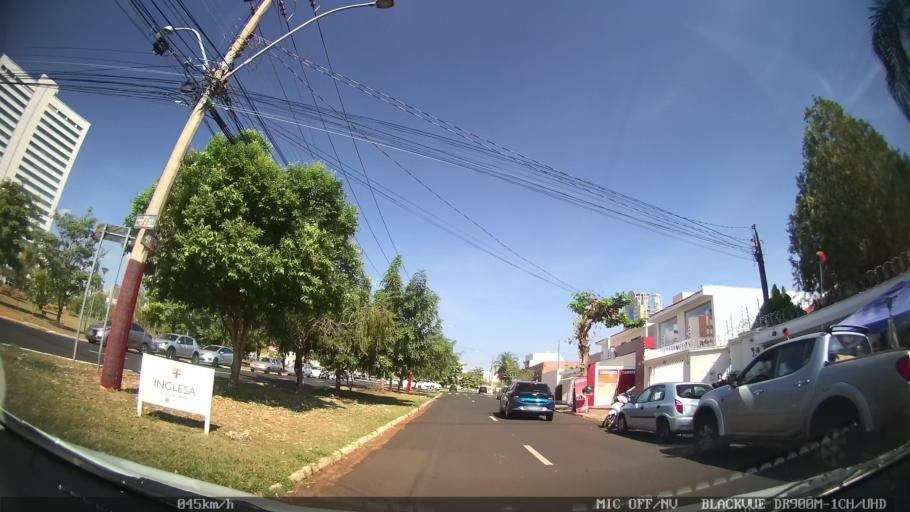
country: BR
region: Sao Paulo
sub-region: Ribeirao Preto
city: Ribeirao Preto
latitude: -21.2086
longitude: -47.8163
